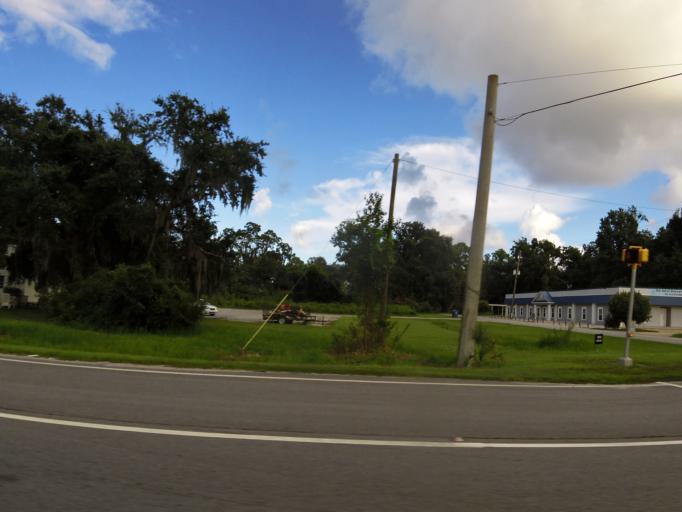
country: US
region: Georgia
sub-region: Glynn County
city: Country Club Estates
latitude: 31.1923
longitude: -81.4690
